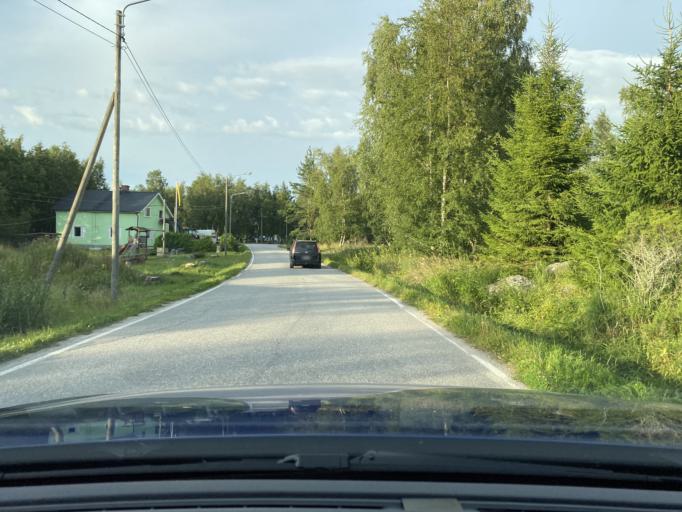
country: FI
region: Ostrobothnia
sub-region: Vaasa
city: Korsnaes
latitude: 62.9743
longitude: 21.1714
